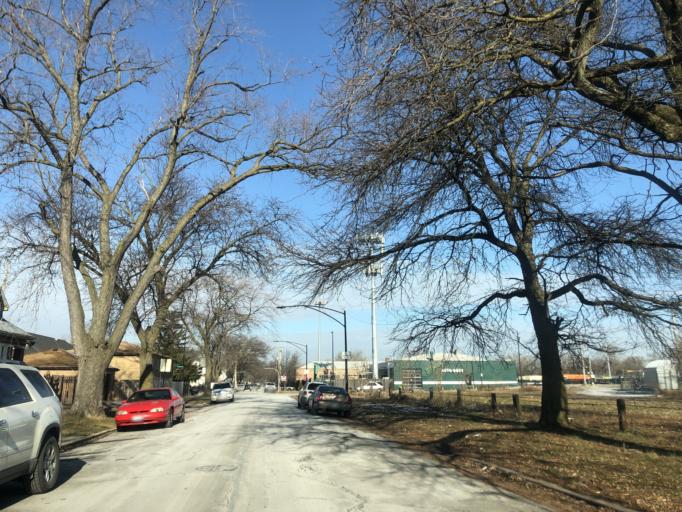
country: US
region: Illinois
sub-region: Cook County
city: Evergreen Park
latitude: 41.7638
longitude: -87.6795
